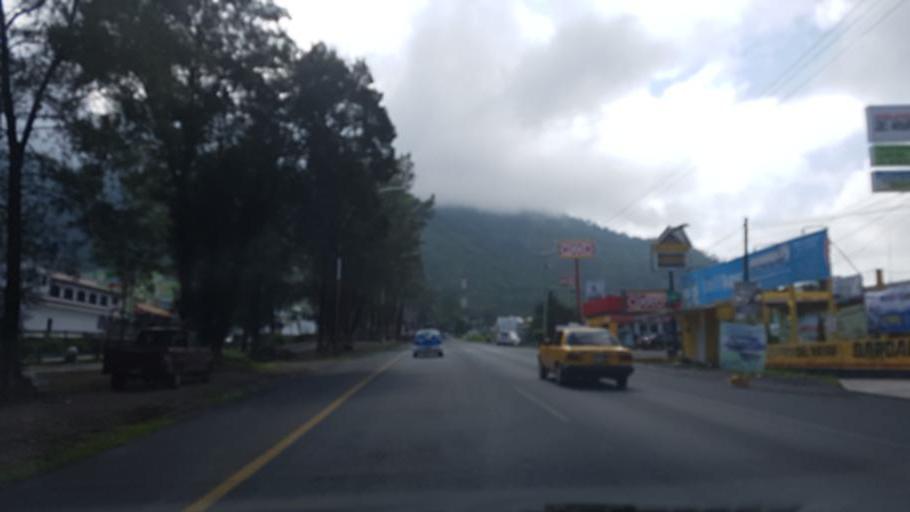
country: MX
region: Nayarit
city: Tepic
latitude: 21.5008
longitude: -104.9132
